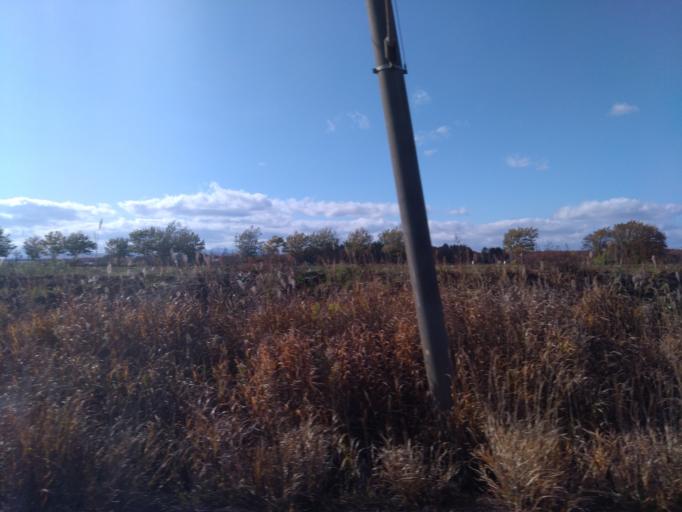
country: JP
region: Hokkaido
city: Kitahiroshima
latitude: 42.9332
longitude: 141.5724
